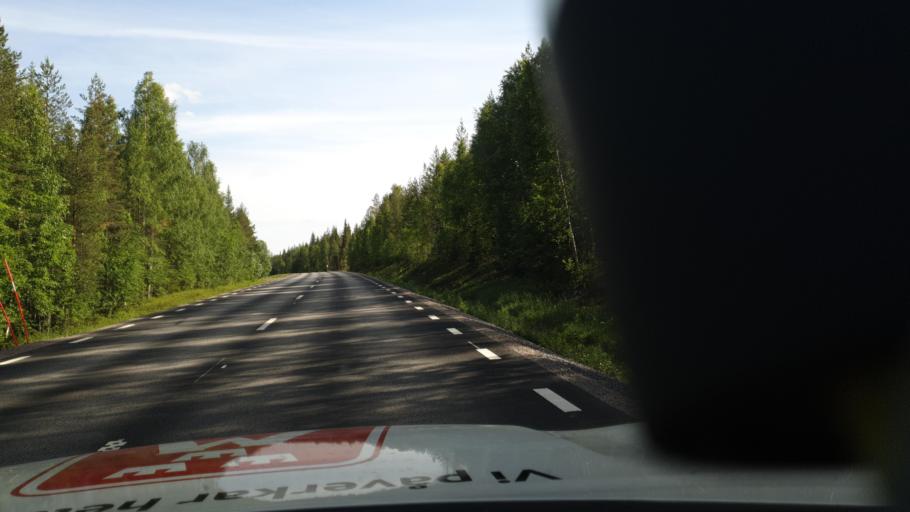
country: SE
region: Vaesterbotten
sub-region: Skelleftea Kommun
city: Boliden
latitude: 64.8928
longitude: 20.3753
